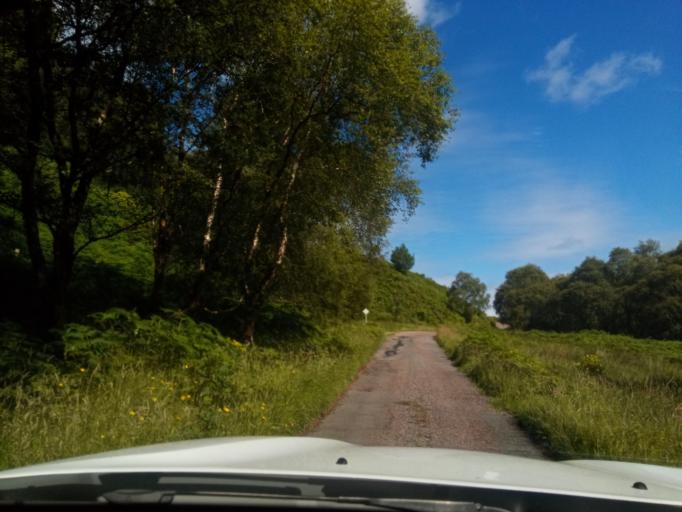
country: GB
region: Scotland
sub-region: Argyll and Bute
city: Isle Of Mull
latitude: 56.7710
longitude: -5.8240
